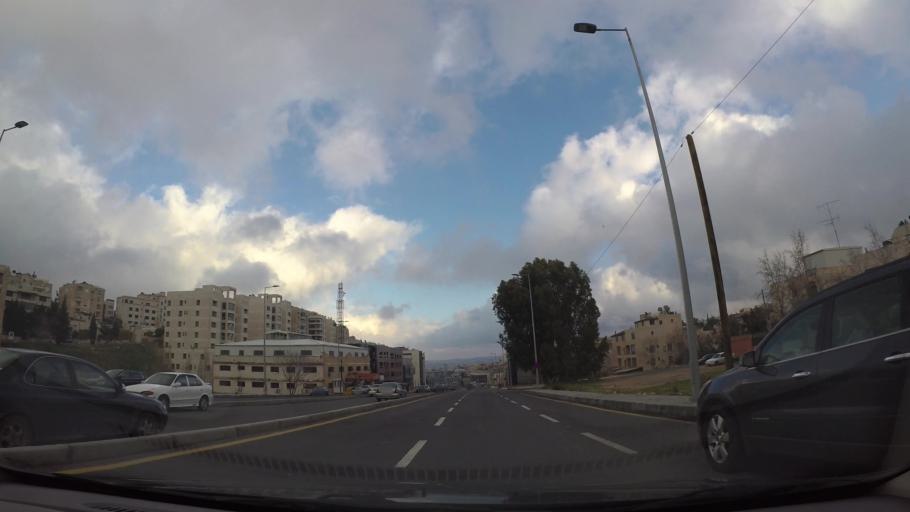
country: JO
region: Amman
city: Wadi as Sir
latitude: 31.9567
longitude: 35.8814
